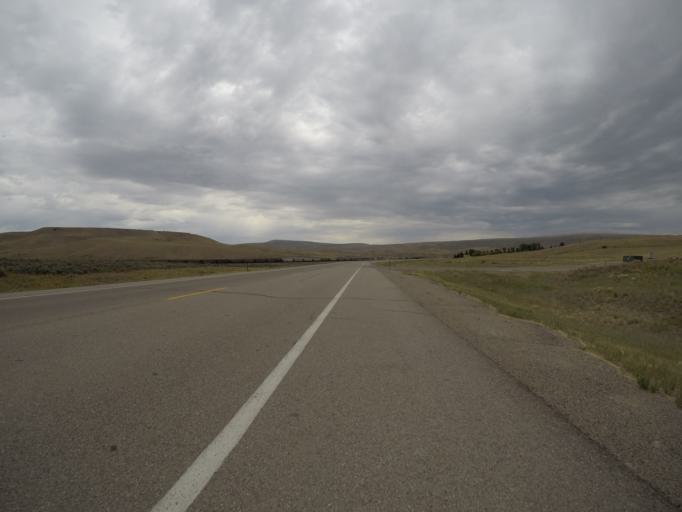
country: US
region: Wyoming
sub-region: Lincoln County
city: Kemmerer
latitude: 41.8000
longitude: -110.5596
